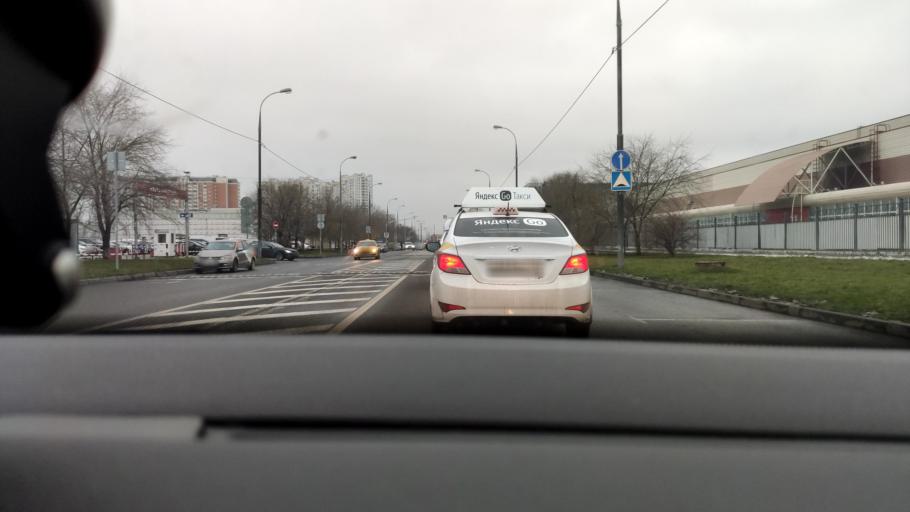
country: RU
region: Moscow
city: Kuz'minki
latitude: 55.6728
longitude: 37.7847
